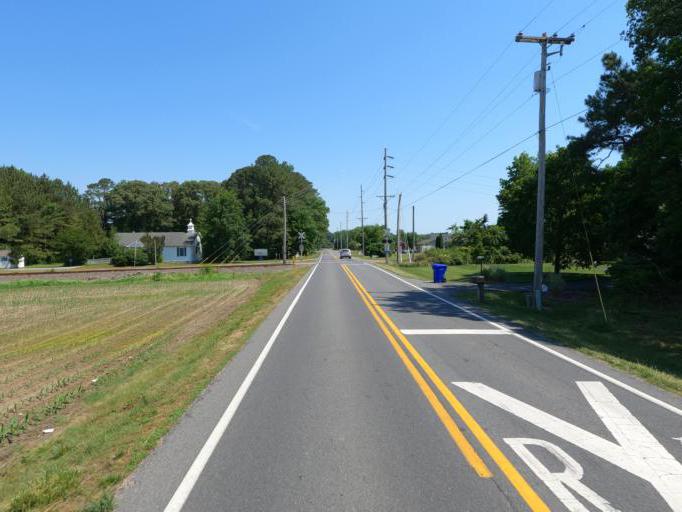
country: US
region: Delaware
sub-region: Sussex County
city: Georgetown
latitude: 38.7013
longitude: -75.3437
